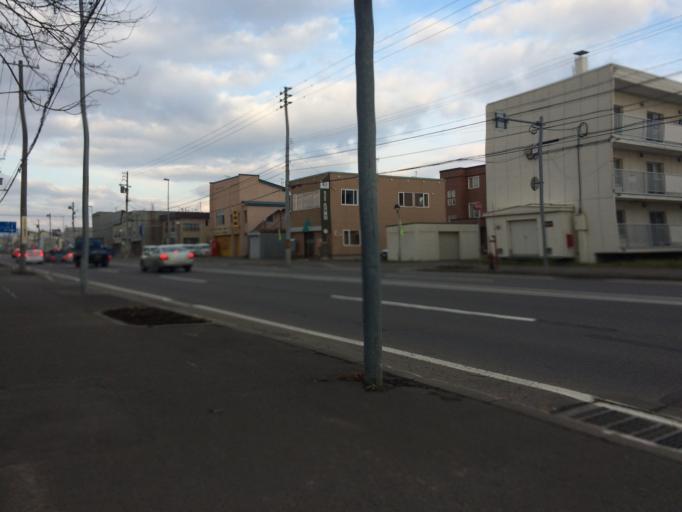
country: JP
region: Hokkaido
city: Niseko Town
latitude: 42.8973
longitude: 140.7523
